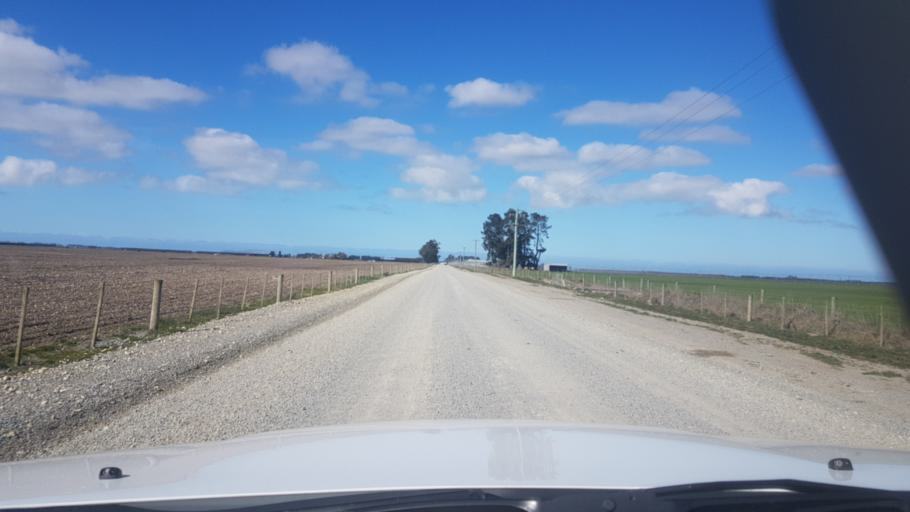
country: NZ
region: Canterbury
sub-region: Timaru District
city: Pleasant Point
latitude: -44.1315
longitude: 171.4059
